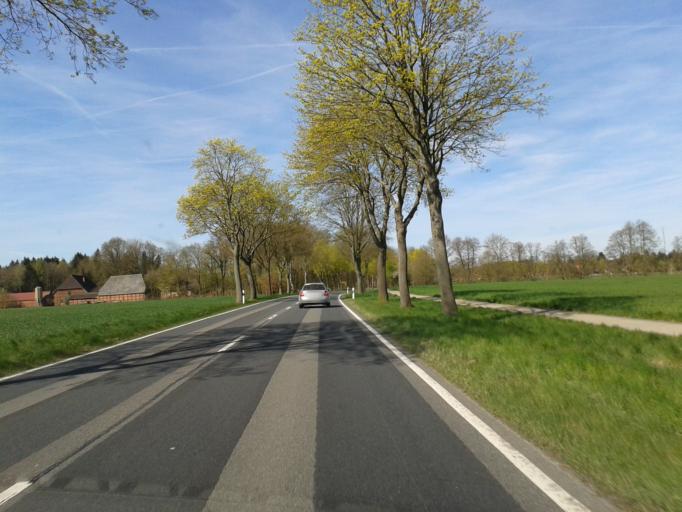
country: DE
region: Lower Saxony
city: Gerdau
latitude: 52.9658
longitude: 10.4035
